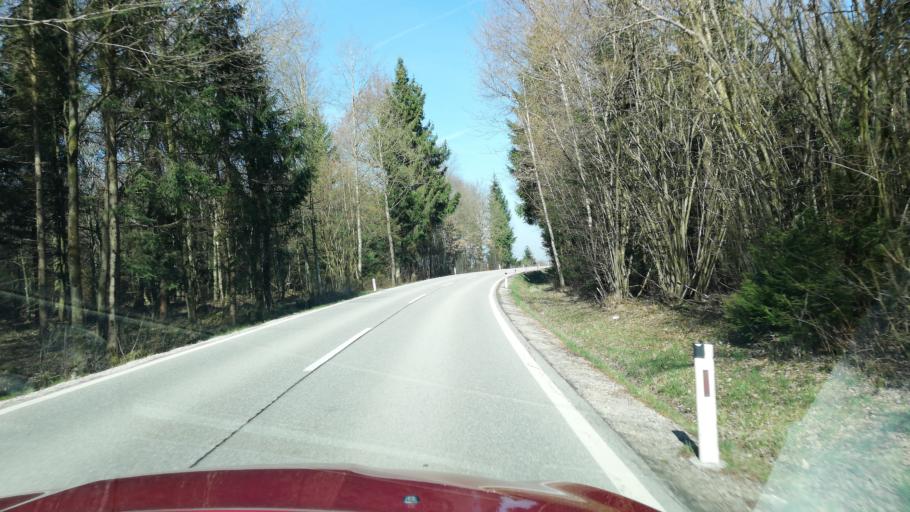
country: AT
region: Upper Austria
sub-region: Politischer Bezirk Kirchdorf an der Krems
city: Kremsmunster
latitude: 48.0819
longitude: 14.1151
